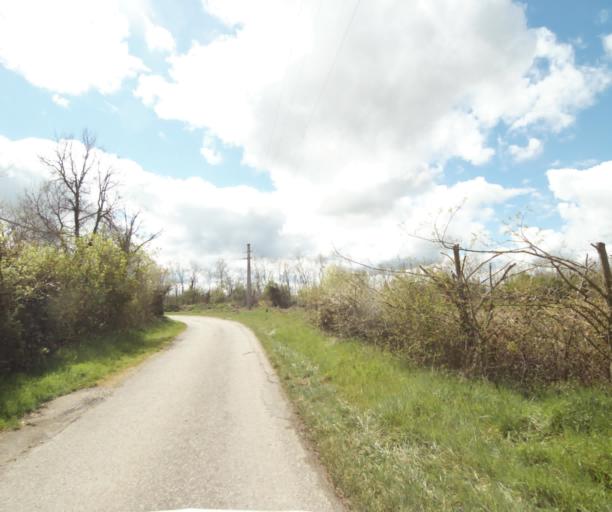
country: FR
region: Midi-Pyrenees
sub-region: Departement de l'Ariege
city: Saverdun
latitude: 43.2595
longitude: 1.5963
